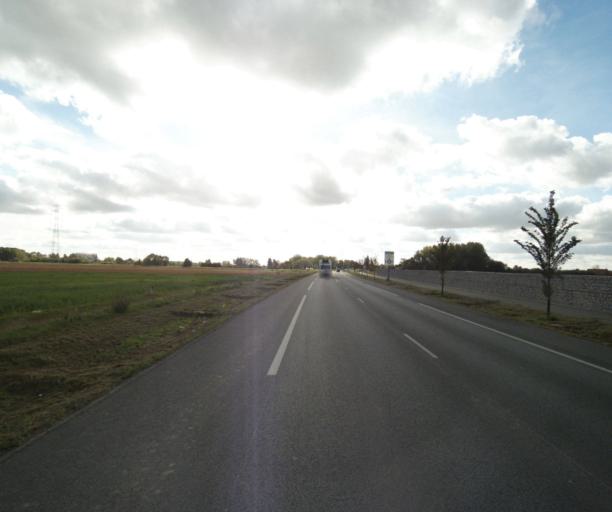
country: FR
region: Nord-Pas-de-Calais
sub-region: Departement du Nord
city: Armentieres
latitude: 50.6638
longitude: 2.9051
